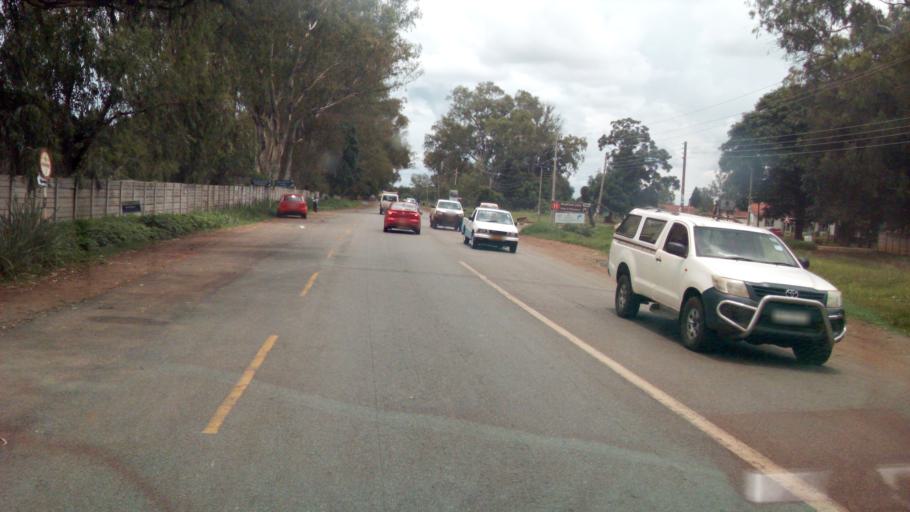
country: ZW
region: Harare
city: Harare
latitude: -17.7504
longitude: 31.0281
